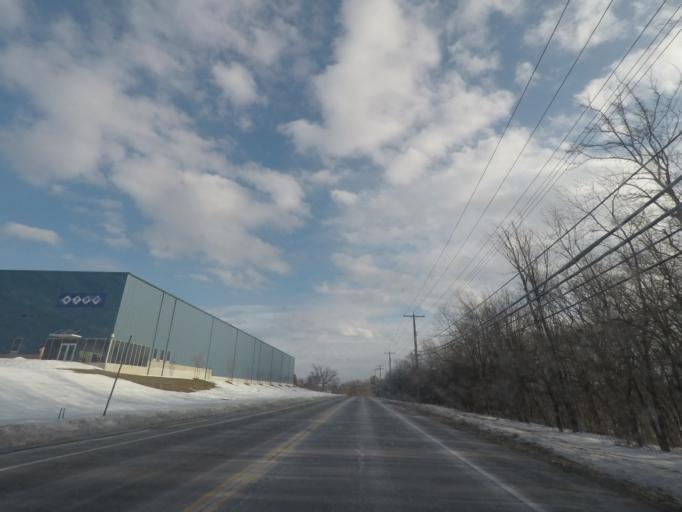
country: US
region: New York
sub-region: Schenectady County
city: Scotia
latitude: 42.8355
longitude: -73.9867
